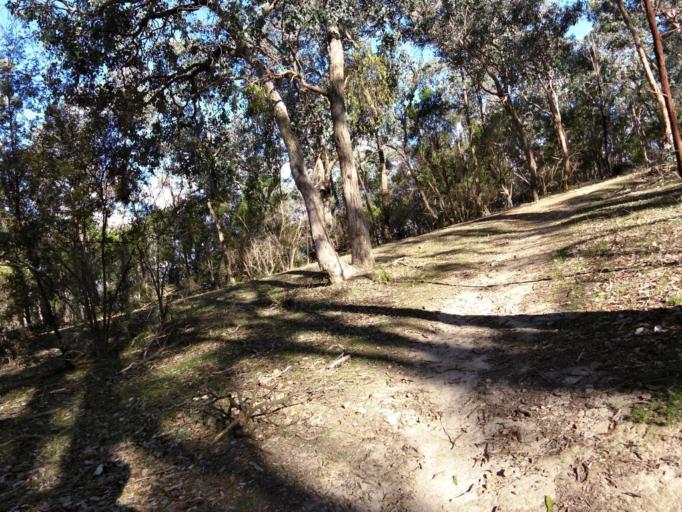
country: AU
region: Victoria
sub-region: Nillumbik
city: North Warrandyte
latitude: -37.7348
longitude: 145.2080
